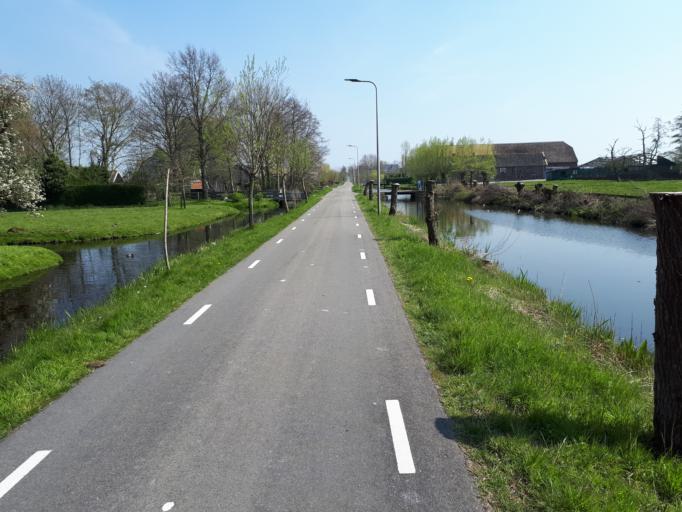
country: NL
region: South Holland
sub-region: Gemeente Nieuwkoop
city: Nieuwkoop
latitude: 52.1315
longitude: 4.7472
